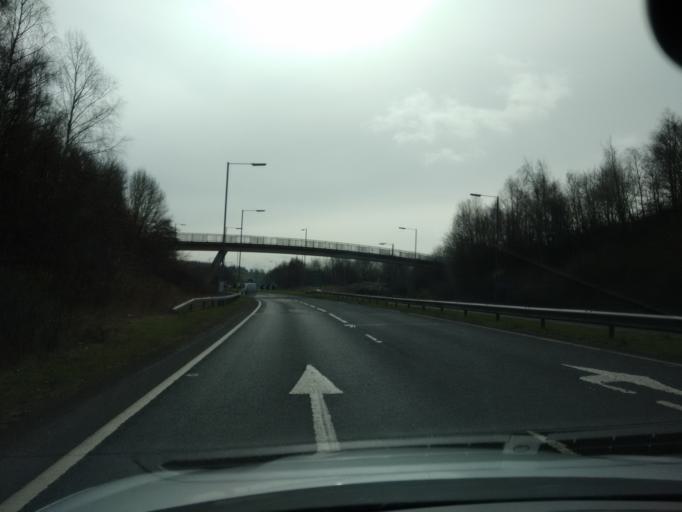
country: GB
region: England
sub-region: Warwickshire
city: Alcester
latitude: 52.2105
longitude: -1.8808
